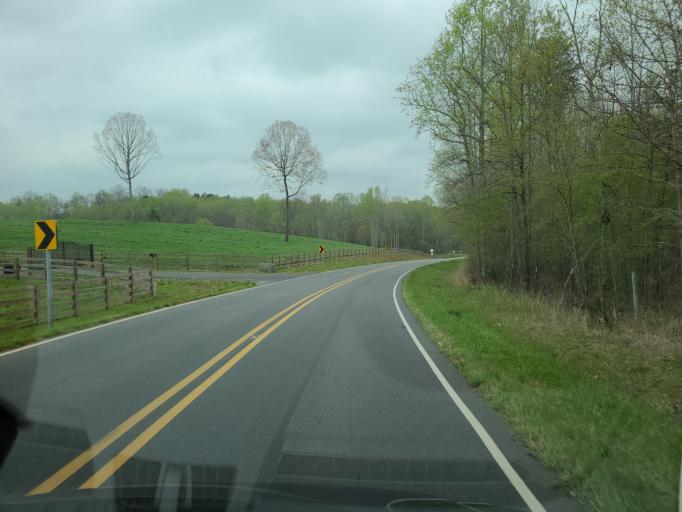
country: US
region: North Carolina
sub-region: Gaston County
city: Cherryville
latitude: 35.4219
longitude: -81.4571
